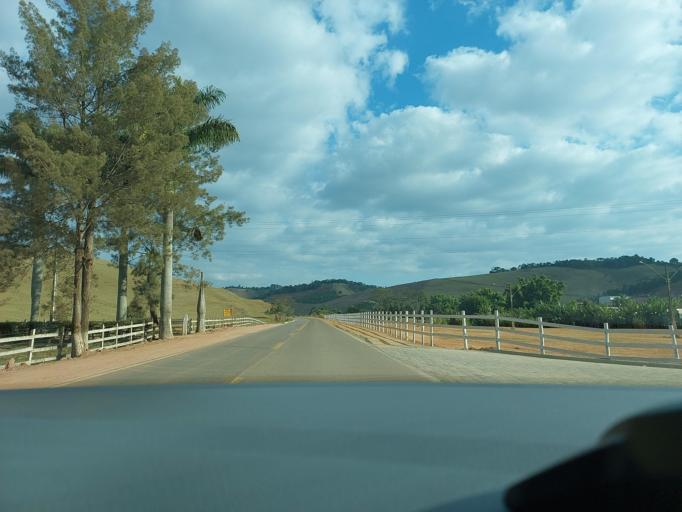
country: BR
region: Minas Gerais
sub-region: Visconde Do Rio Branco
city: Visconde do Rio Branco
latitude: -20.8611
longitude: -42.6696
